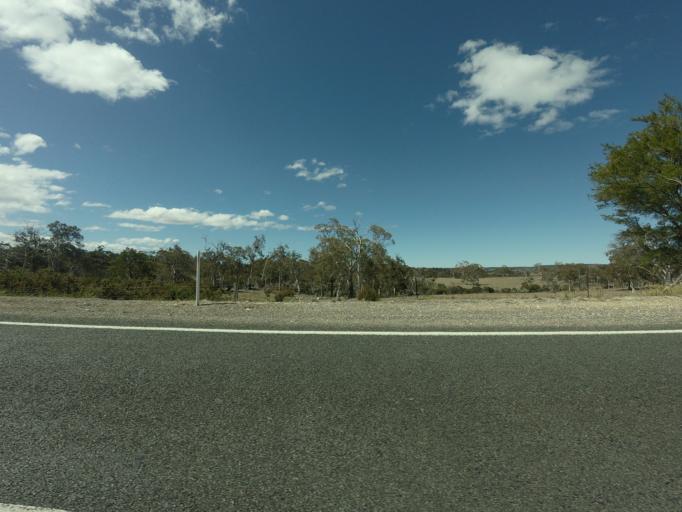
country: AU
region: Tasmania
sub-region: Break O'Day
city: St Helens
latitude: -42.0256
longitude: 148.0183
